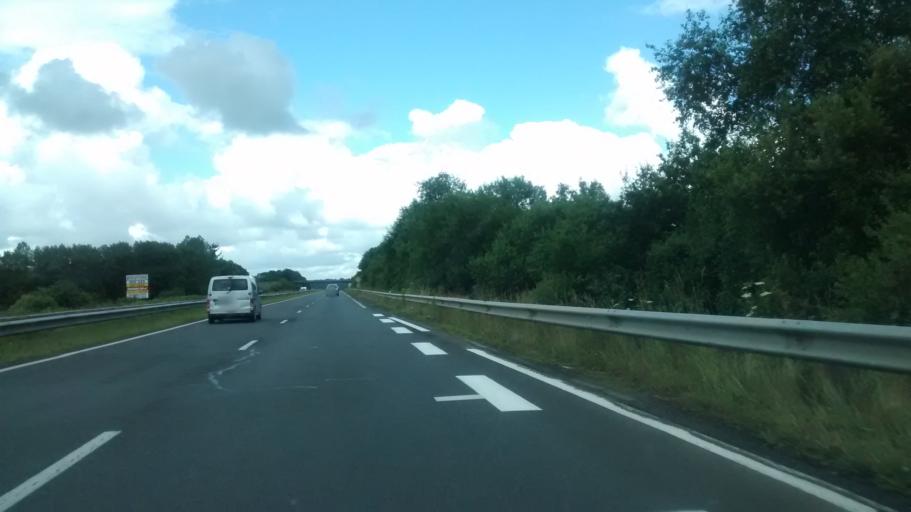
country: FR
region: Brittany
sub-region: Departement des Cotes-d'Armor
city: Belle-Isle-en-Terre
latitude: 48.5523
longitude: -3.3779
